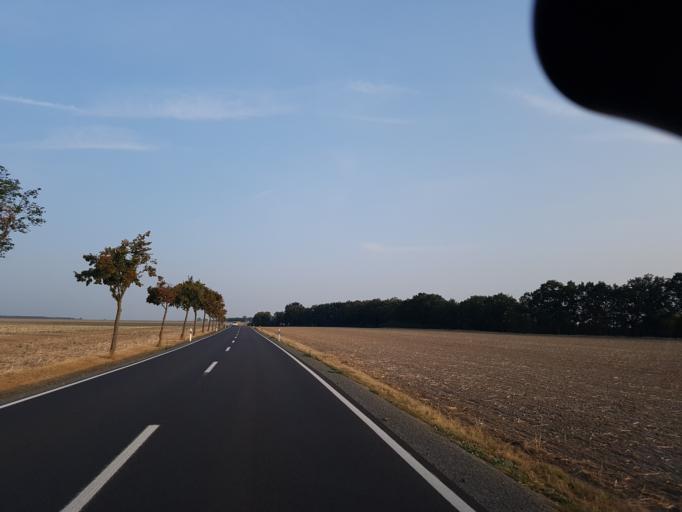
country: DE
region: Saxony
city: Zinna
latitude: 51.5842
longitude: 12.9567
